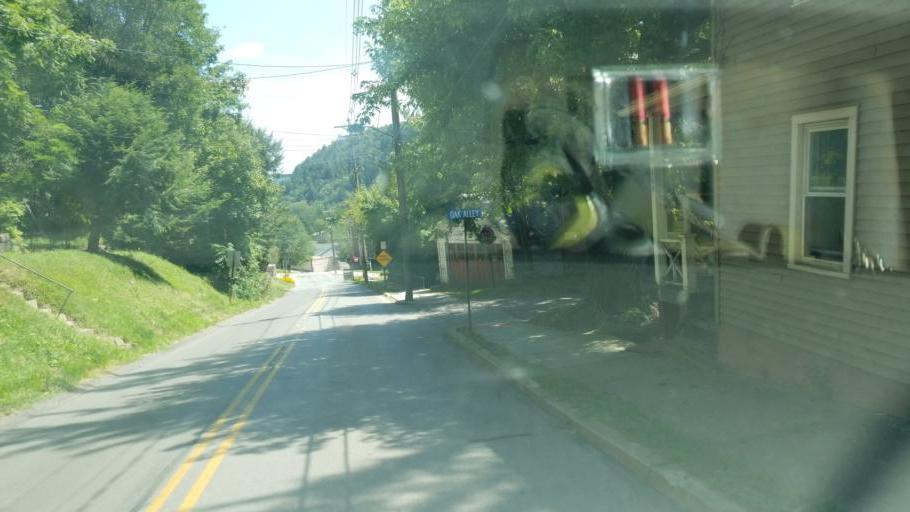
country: US
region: Pennsylvania
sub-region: Clarion County
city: Knox
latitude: 41.1786
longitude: -79.7104
